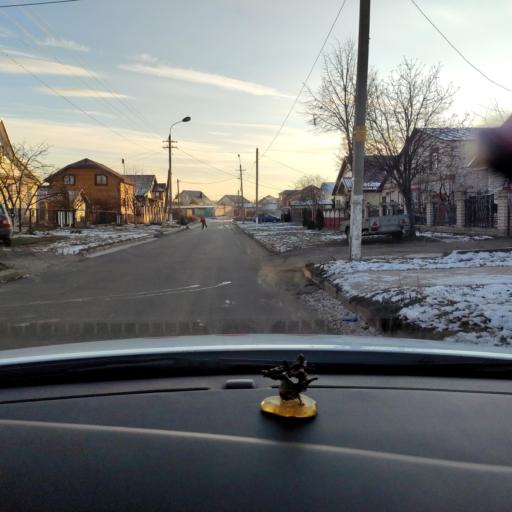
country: RU
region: Tatarstan
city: Stolbishchi
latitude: 55.6100
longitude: 49.1364
